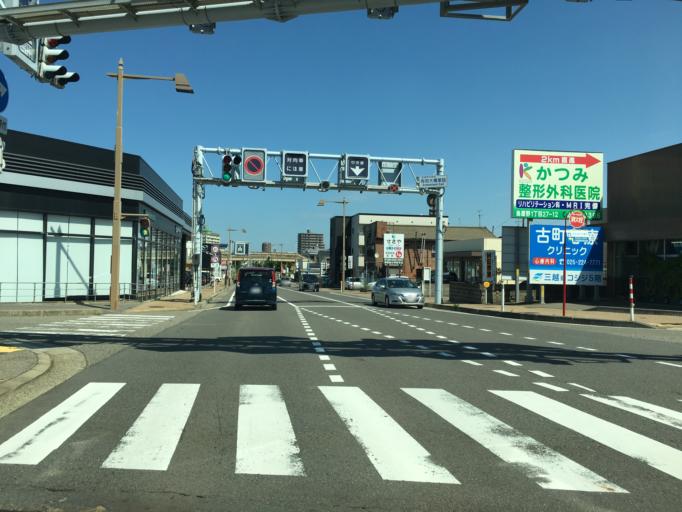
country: JP
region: Niigata
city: Niigata-shi
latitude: 37.9027
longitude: 139.0086
